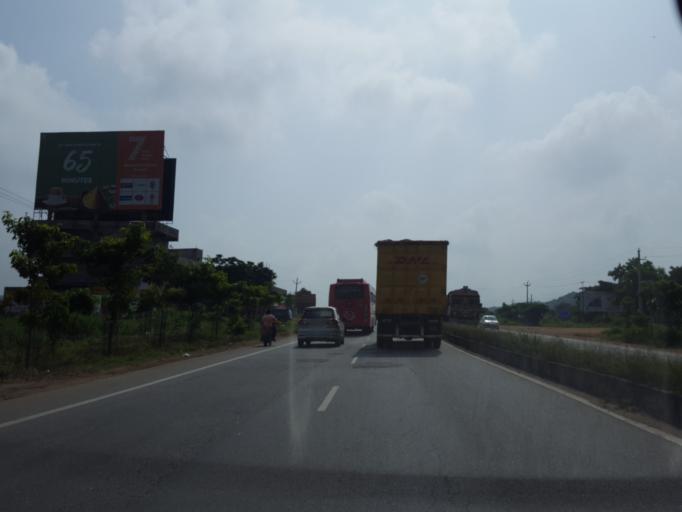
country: IN
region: Telangana
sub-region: Rangareddi
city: Ghatkesar
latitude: 17.2893
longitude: 78.7679
